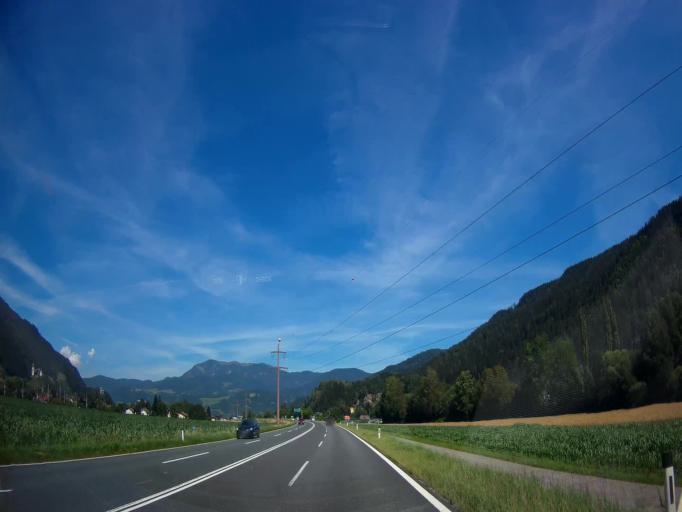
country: AT
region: Carinthia
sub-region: Politischer Bezirk Sankt Veit an der Glan
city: Friesach
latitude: 46.9472
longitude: 14.4218
